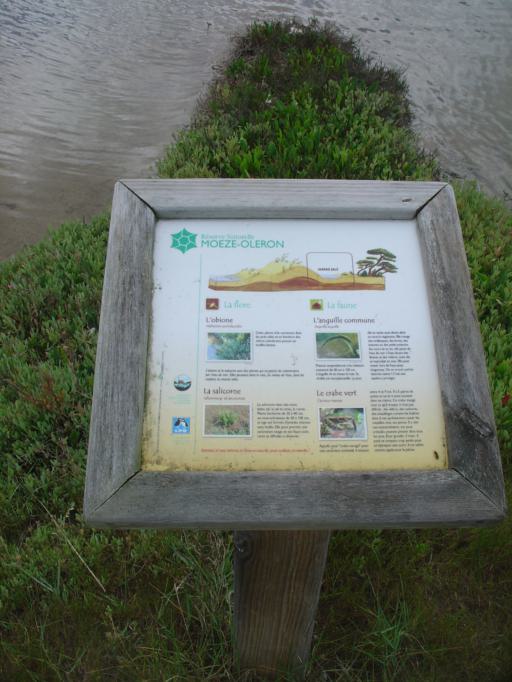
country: FR
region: Poitou-Charentes
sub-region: Departement de la Charente-Maritime
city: Boyard-Ville
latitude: 45.9556
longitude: -1.2422
